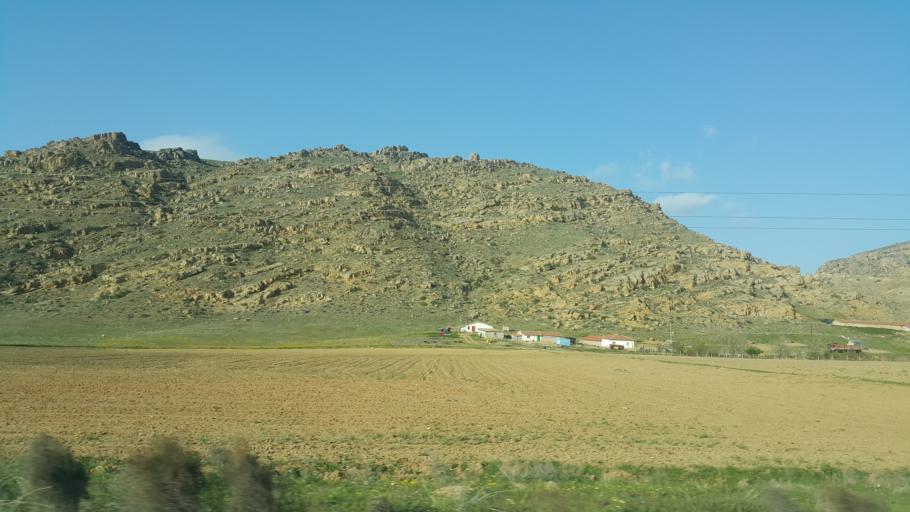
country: TR
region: Ankara
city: Sereflikochisar
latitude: 38.9771
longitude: 33.4946
